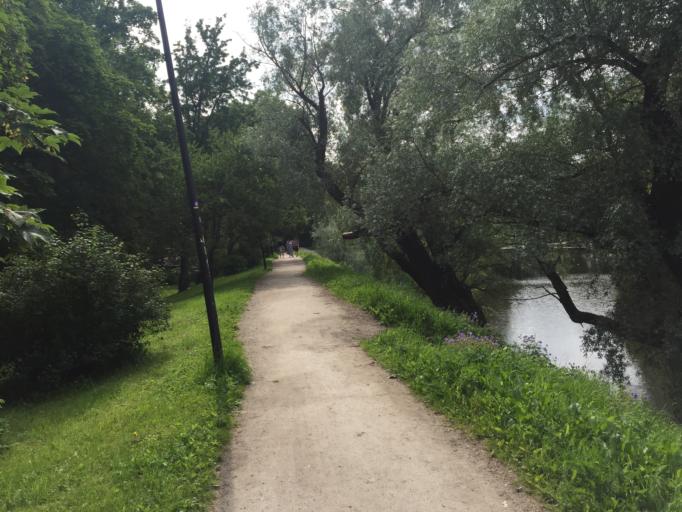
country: EE
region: Harju
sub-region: Tallinna linn
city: Tallinn
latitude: 59.4388
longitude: 24.7396
